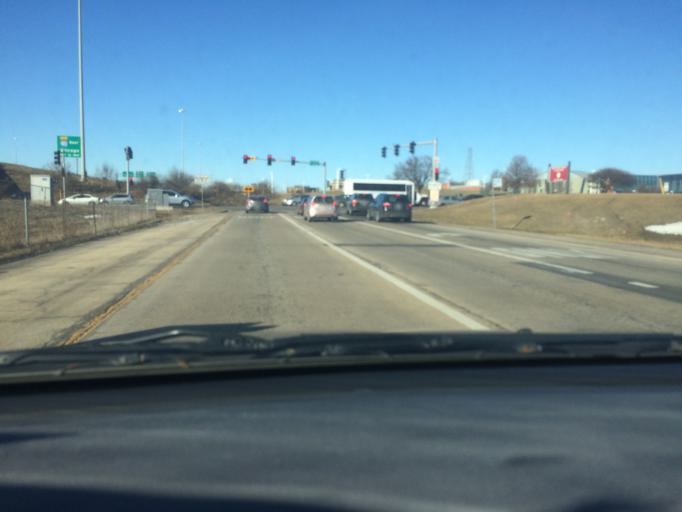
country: US
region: Illinois
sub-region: Cook County
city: Rolling Meadows
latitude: 42.0502
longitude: -88.0281
